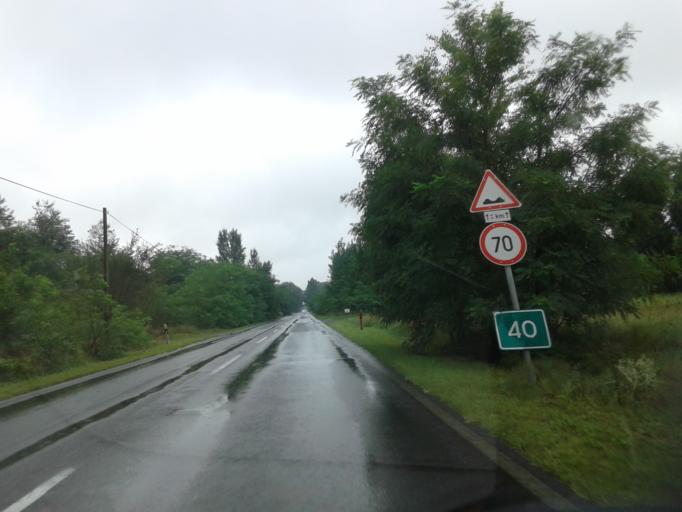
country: HU
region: Bacs-Kiskun
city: Kelebia
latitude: 46.2560
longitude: 19.6639
